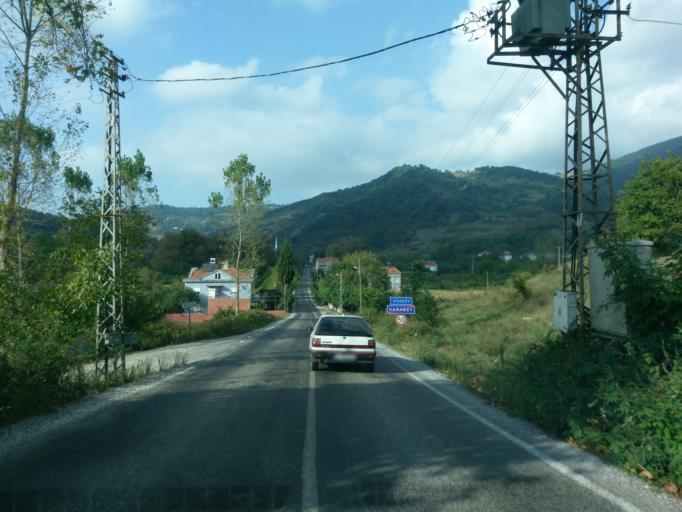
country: TR
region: Sinop
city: Helaldi
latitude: 41.9215
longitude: 34.4137
